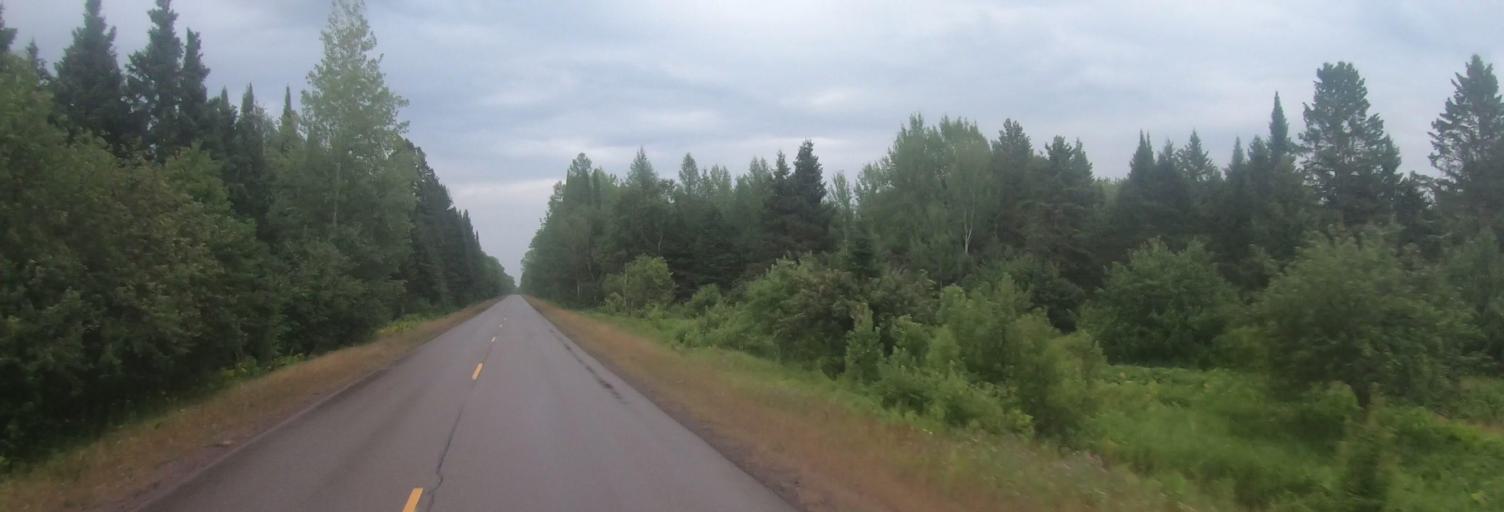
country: US
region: Michigan
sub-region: Keweenaw County
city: Eagle River
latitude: 47.2860
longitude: -88.2967
